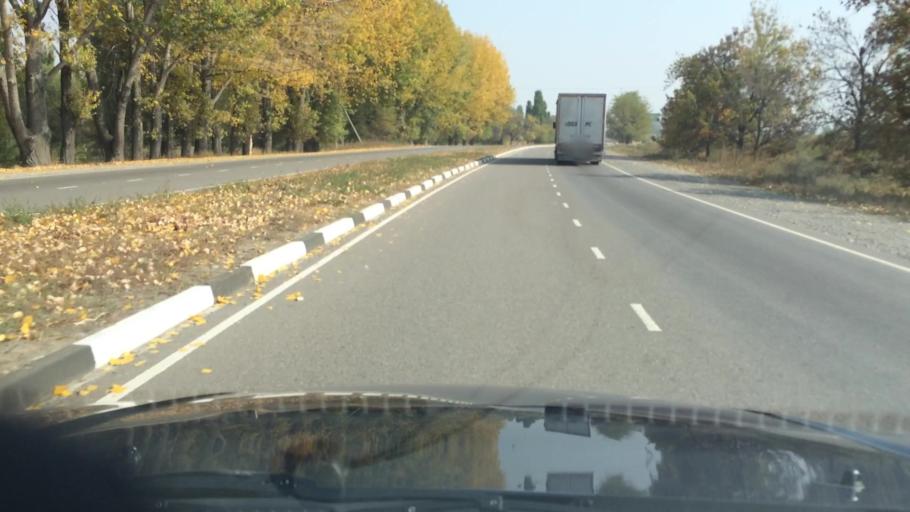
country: KG
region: Chuy
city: Kant
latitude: 42.9736
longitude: 74.8598
